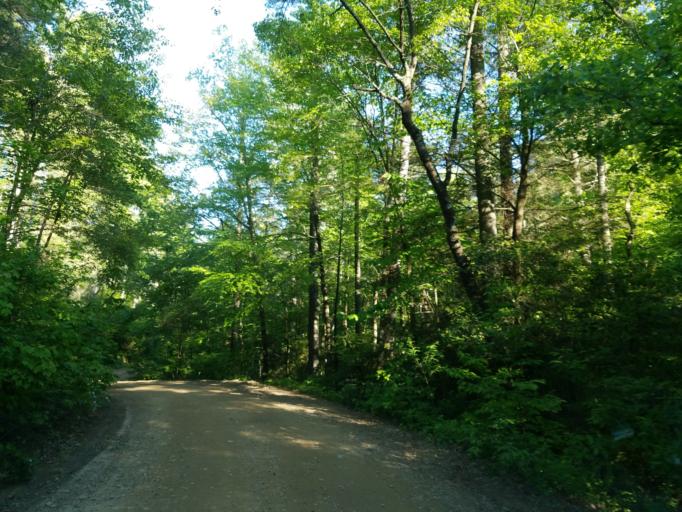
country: US
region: Georgia
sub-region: Lumpkin County
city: Dahlonega
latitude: 34.6938
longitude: -84.1426
